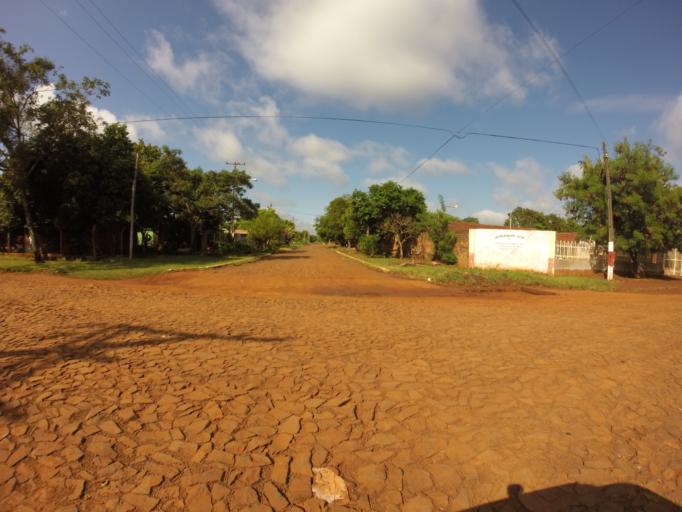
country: PY
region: Alto Parana
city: Ciudad del Este
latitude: -25.3964
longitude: -54.6464
